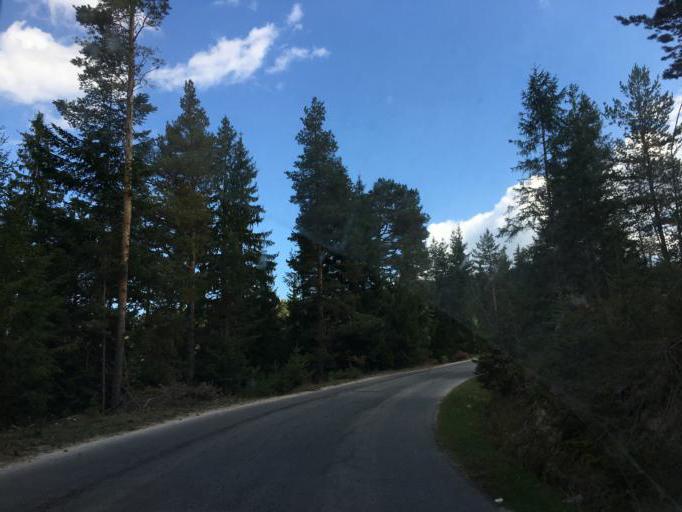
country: BG
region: Pazardzhik
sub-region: Obshtina Batak
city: Batak
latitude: 41.9261
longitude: 24.2800
